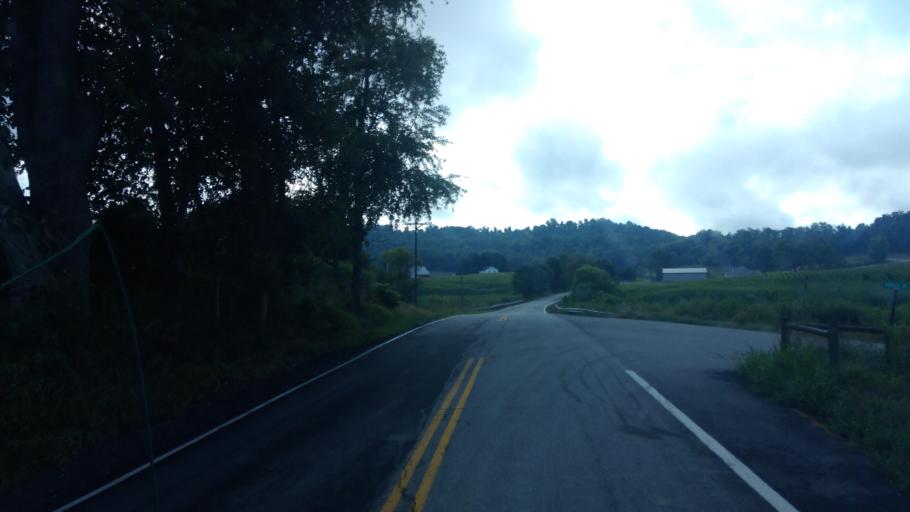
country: US
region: Ohio
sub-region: Belmont County
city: Barnesville
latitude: 40.0988
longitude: -81.3376
